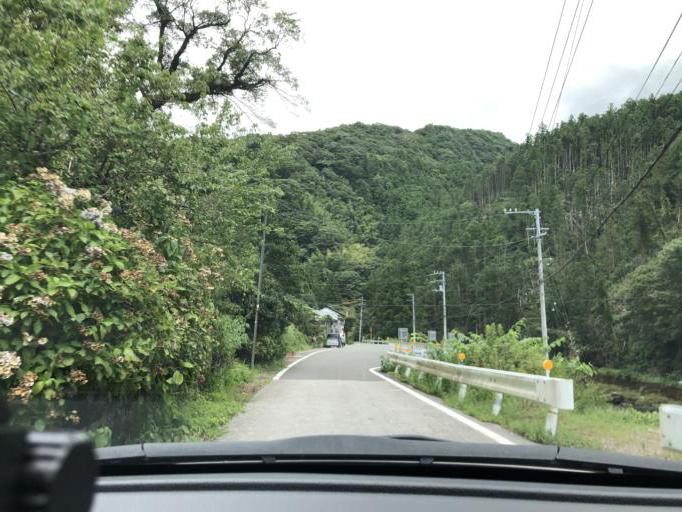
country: JP
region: Kochi
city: Kochi-shi
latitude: 33.6254
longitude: 133.5025
